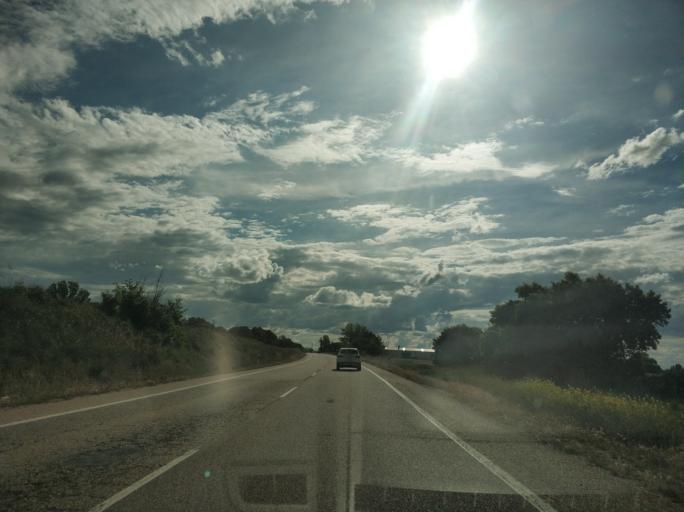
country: ES
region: Castille and Leon
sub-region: Provincia de Burgos
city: Villalba de Duero
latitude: 41.6613
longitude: -3.7551
